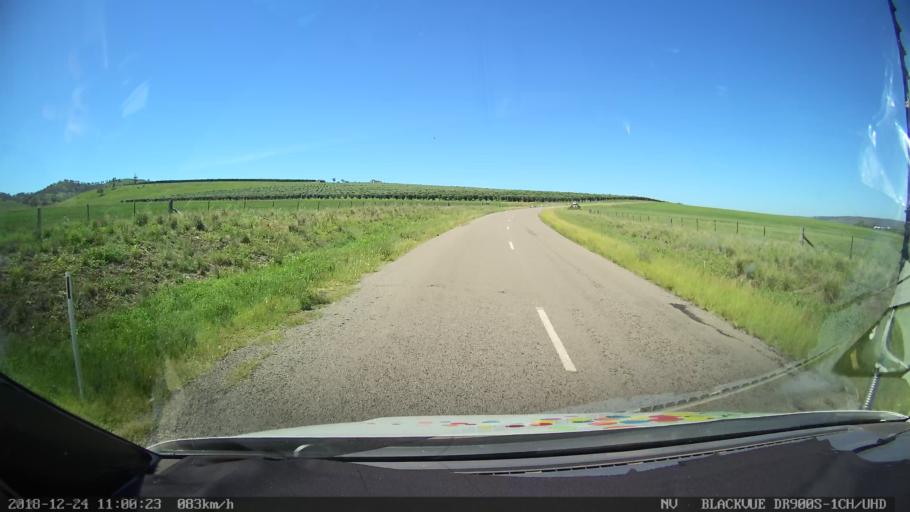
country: AU
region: New South Wales
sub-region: Upper Hunter Shire
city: Merriwa
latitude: -32.0670
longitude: 150.3942
